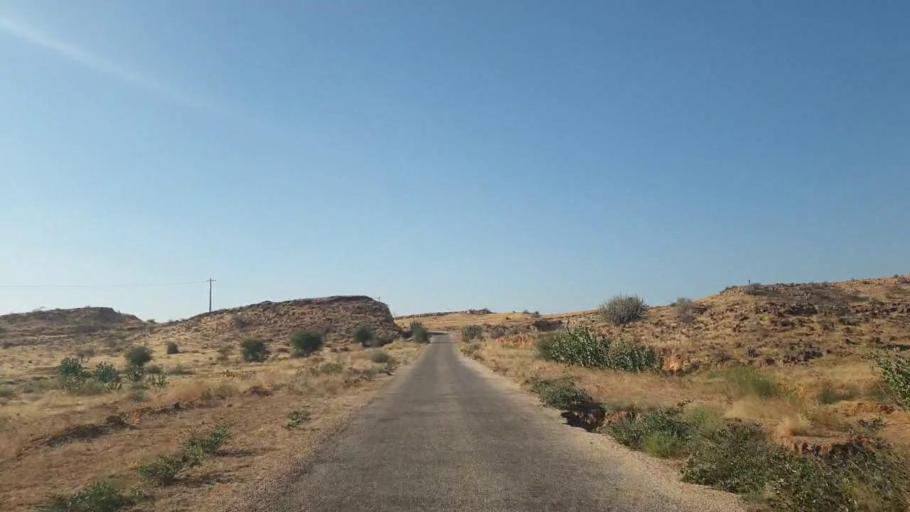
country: PK
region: Sindh
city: Malir Cantonment
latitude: 25.4016
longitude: 67.4885
